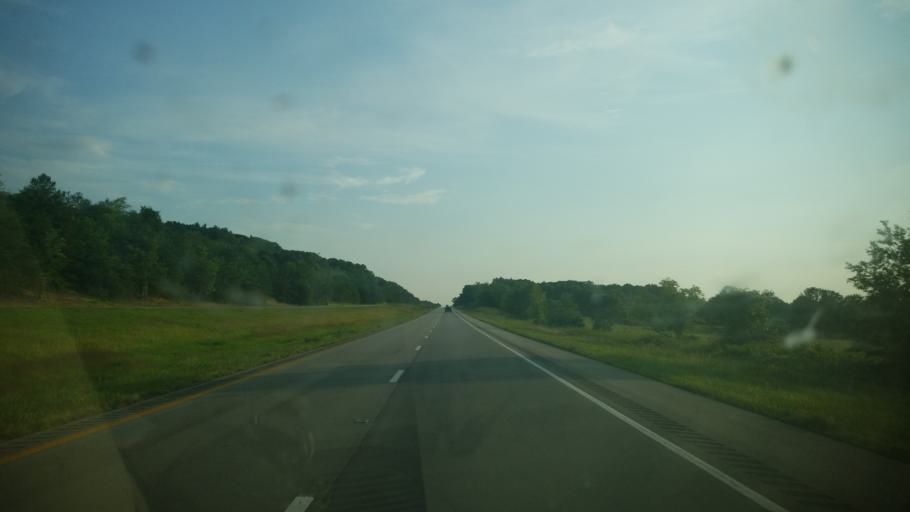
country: US
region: Ohio
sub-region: Adams County
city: Peebles
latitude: 38.9894
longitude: -83.3137
